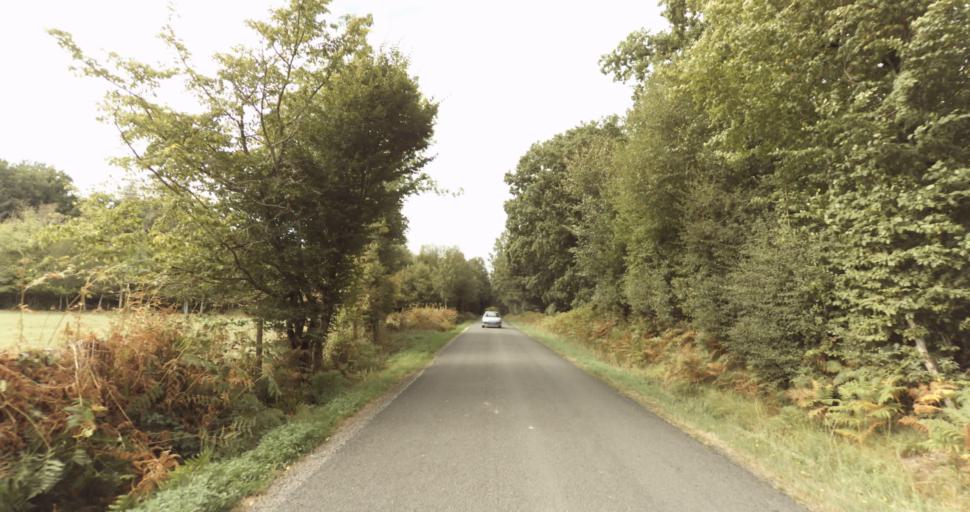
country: FR
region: Lower Normandy
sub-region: Departement de l'Orne
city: Sainte-Gauburge-Sainte-Colombe
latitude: 48.7808
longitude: 0.3868
